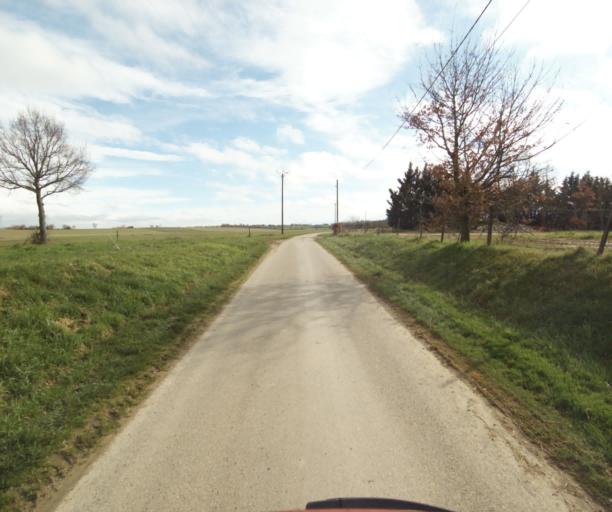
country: FR
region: Midi-Pyrenees
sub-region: Departement de l'Ariege
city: La Tour-du-Crieu
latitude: 43.1382
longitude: 1.6977
